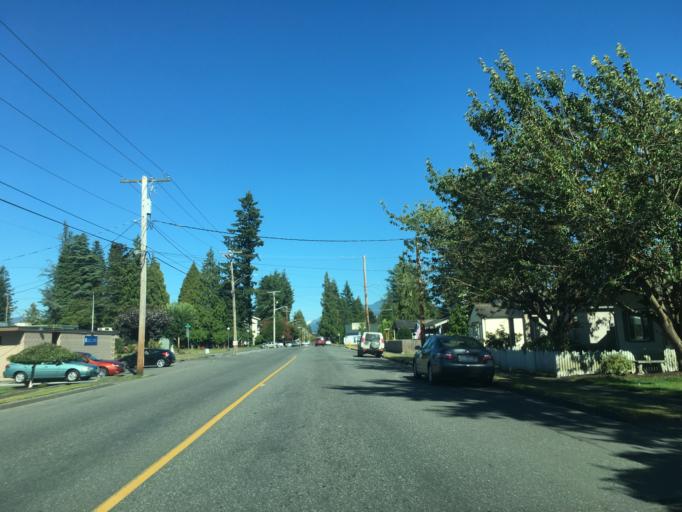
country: US
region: Washington
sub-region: Skagit County
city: Sedro-Woolley
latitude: 48.5033
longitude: -122.2294
